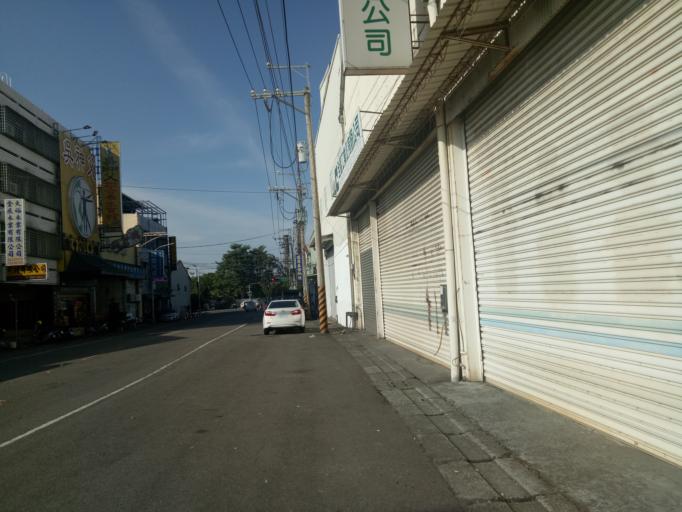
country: TW
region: Taiwan
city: Fengyuan
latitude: 24.2581
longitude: 120.7332
